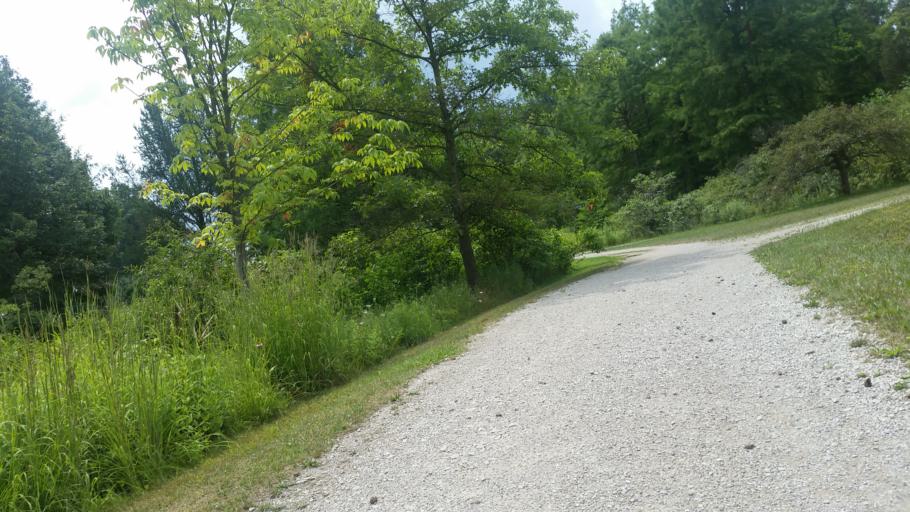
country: US
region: Ohio
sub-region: Lake County
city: Kirtland
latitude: 41.6098
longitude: -81.3031
